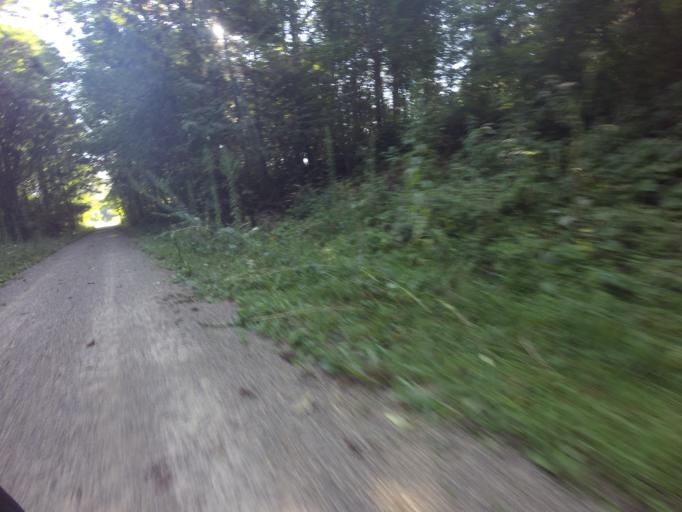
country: CA
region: Ontario
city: Huron East
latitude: 43.7382
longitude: -81.4485
